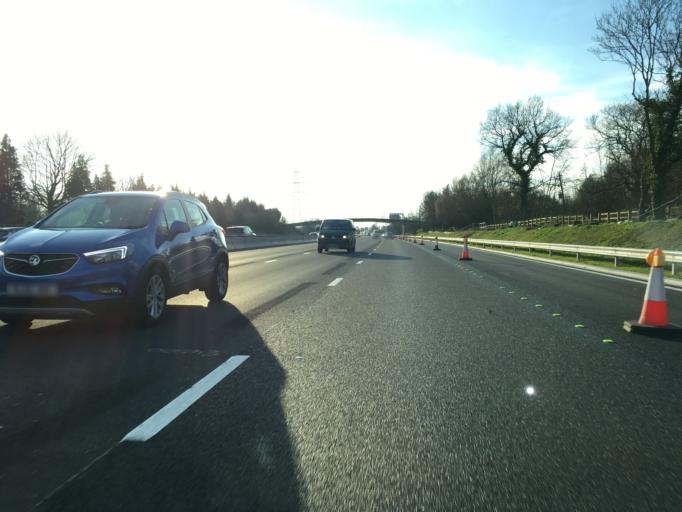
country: GB
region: England
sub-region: Cheshire East
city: Knutsford
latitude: 53.2647
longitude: -2.4017
